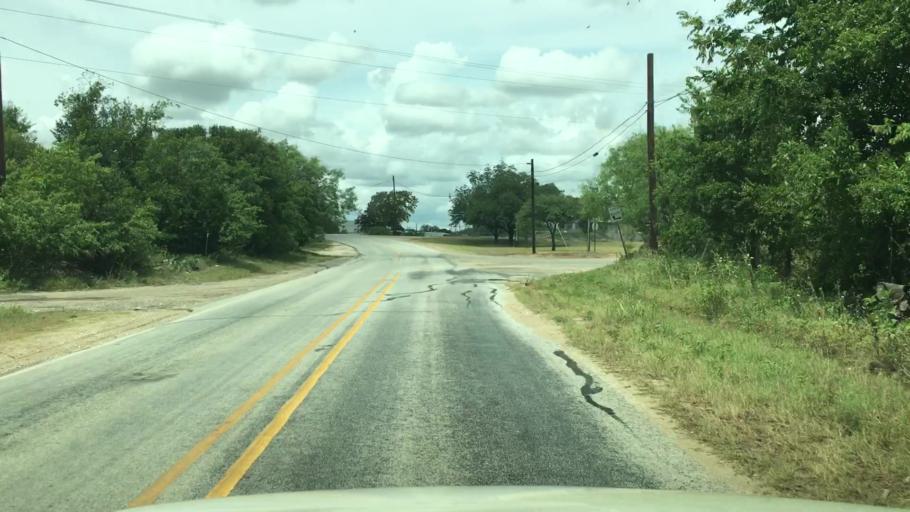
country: US
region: Texas
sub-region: McCulloch County
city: Brady
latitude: 31.1219
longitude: -99.3235
